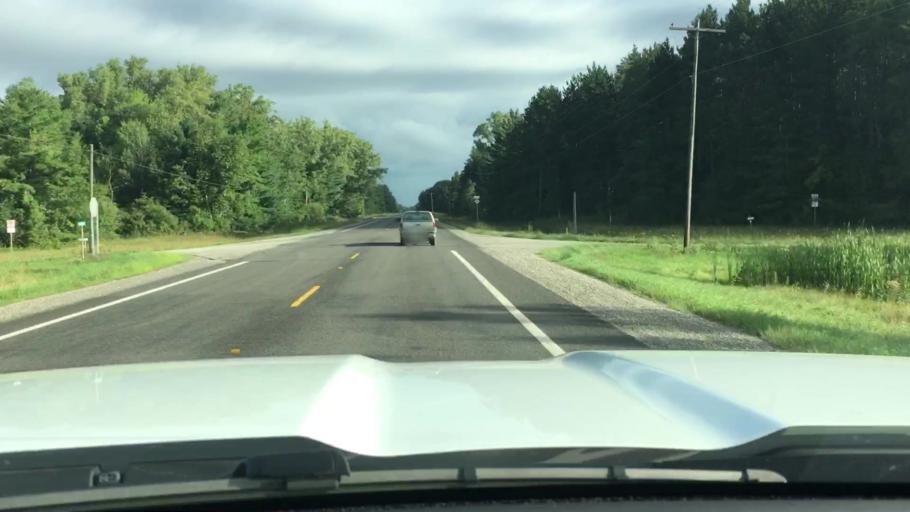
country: US
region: Michigan
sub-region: Tuscola County
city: Caro
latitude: 43.4233
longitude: -83.3845
